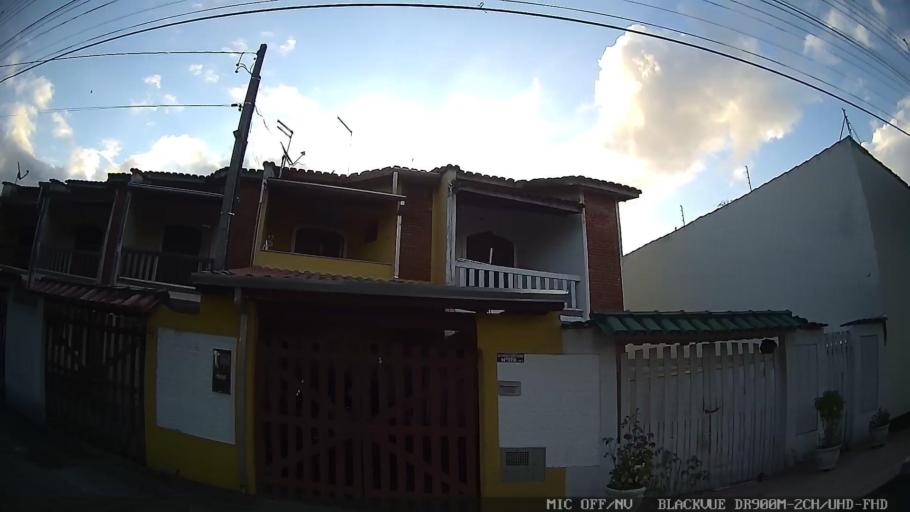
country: BR
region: Sao Paulo
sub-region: Caraguatatuba
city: Caraguatatuba
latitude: -23.6630
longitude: -45.4399
